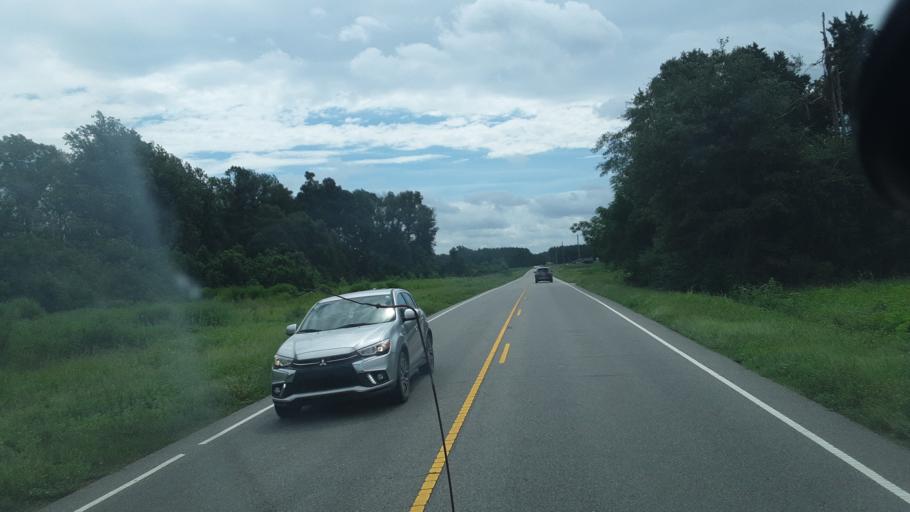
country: US
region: North Carolina
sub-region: Robeson County
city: Maxton
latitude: 34.6316
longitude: -79.3398
